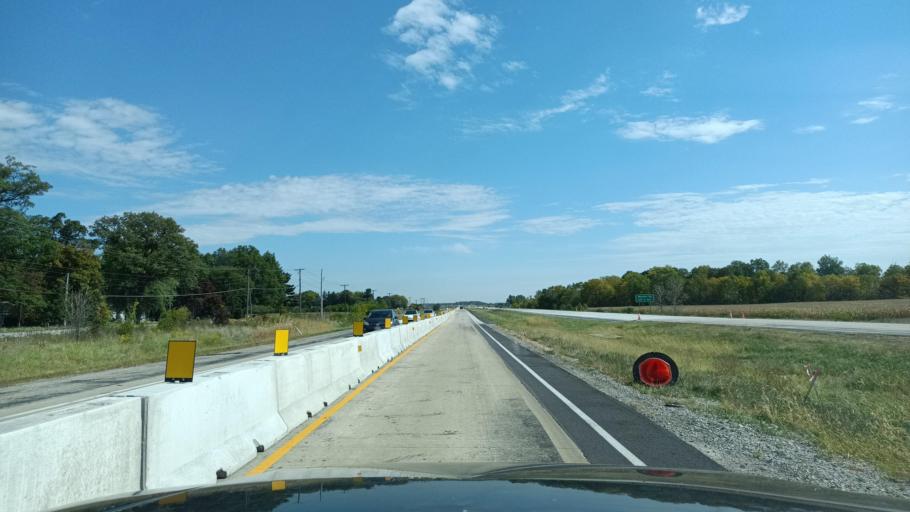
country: US
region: Indiana
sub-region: Allen County
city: New Haven
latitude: 41.1077
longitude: -84.9544
